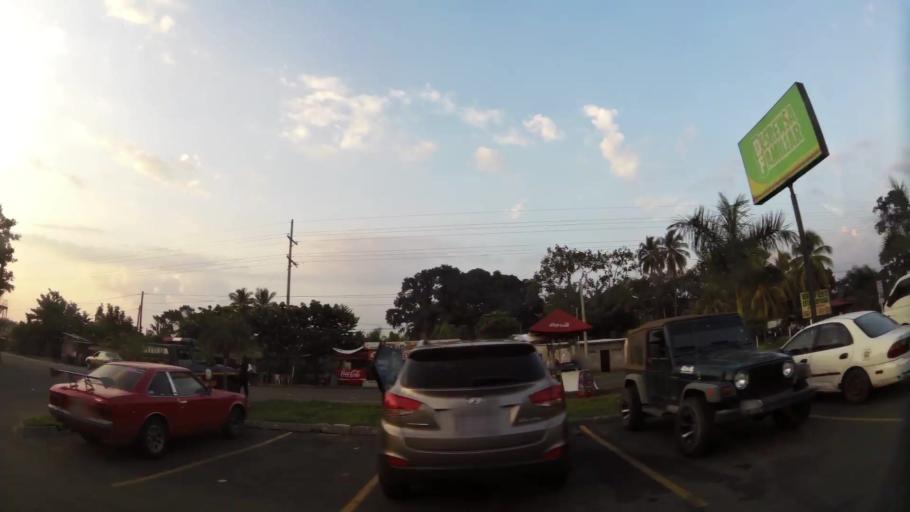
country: GT
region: Retalhuleu
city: San Sebastian
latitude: 14.5733
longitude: -91.6488
